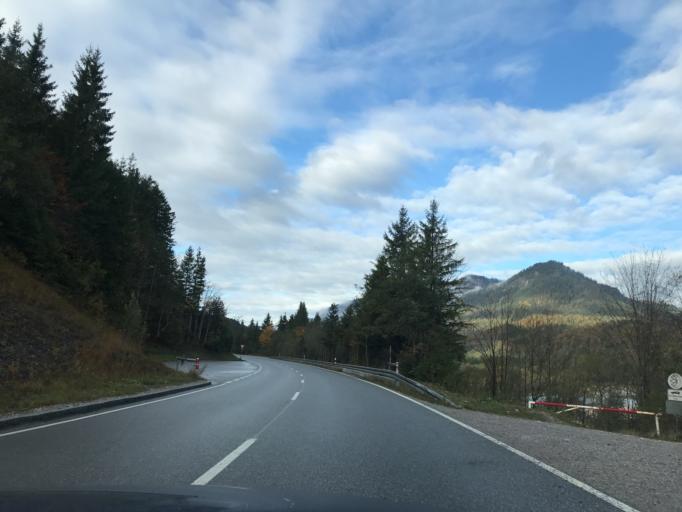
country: DE
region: Bavaria
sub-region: Upper Bavaria
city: Jachenau
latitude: 47.5604
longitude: 11.5030
